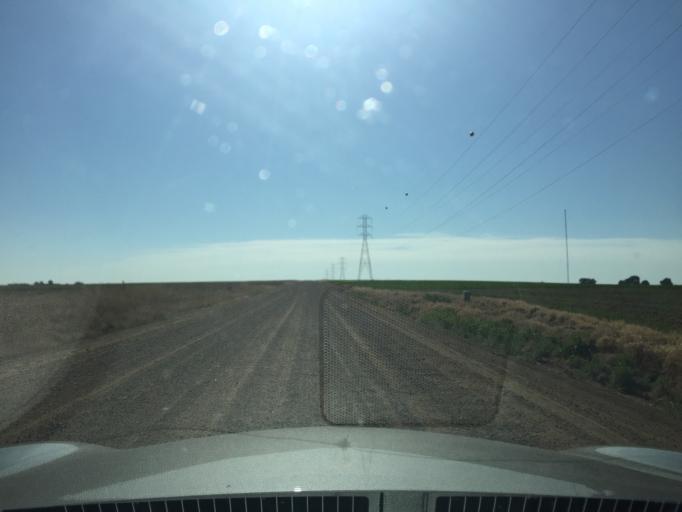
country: US
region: Colorado
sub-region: Boulder County
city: Erie
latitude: 40.0583
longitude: -105.0289
